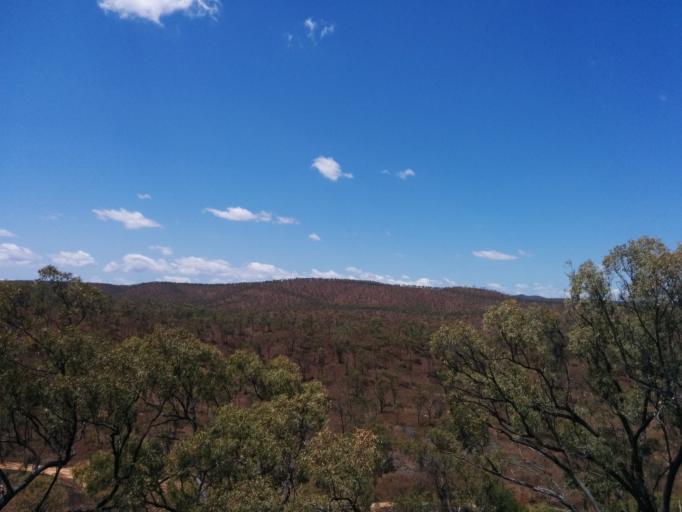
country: AU
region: Queensland
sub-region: Tablelands
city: Mareeba
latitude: -16.9210
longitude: 145.0296
